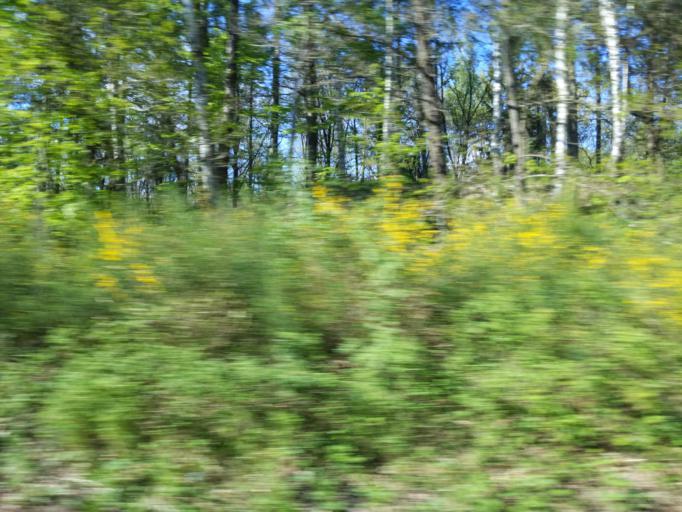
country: DE
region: Saxony
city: Radeberg
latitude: 51.1228
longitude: 13.8665
